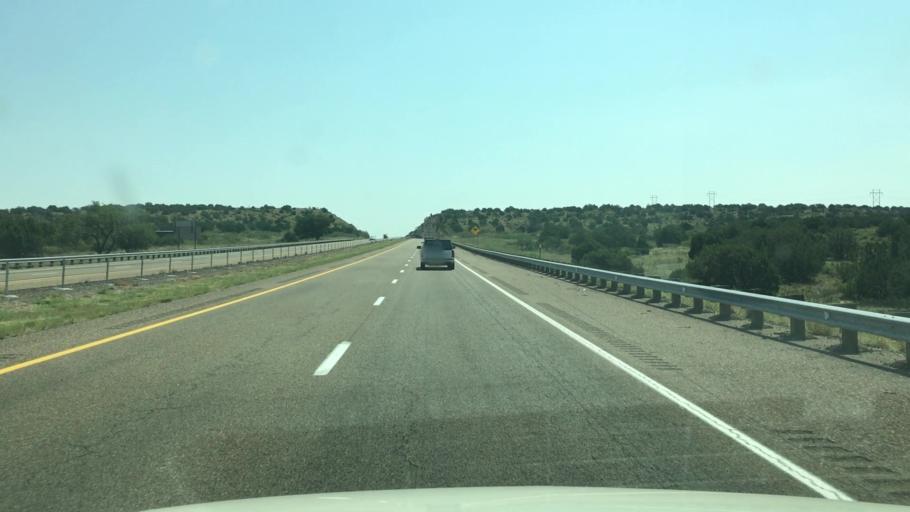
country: US
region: New Mexico
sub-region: Quay County
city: Tucumcari
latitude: 35.1170
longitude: -103.8810
